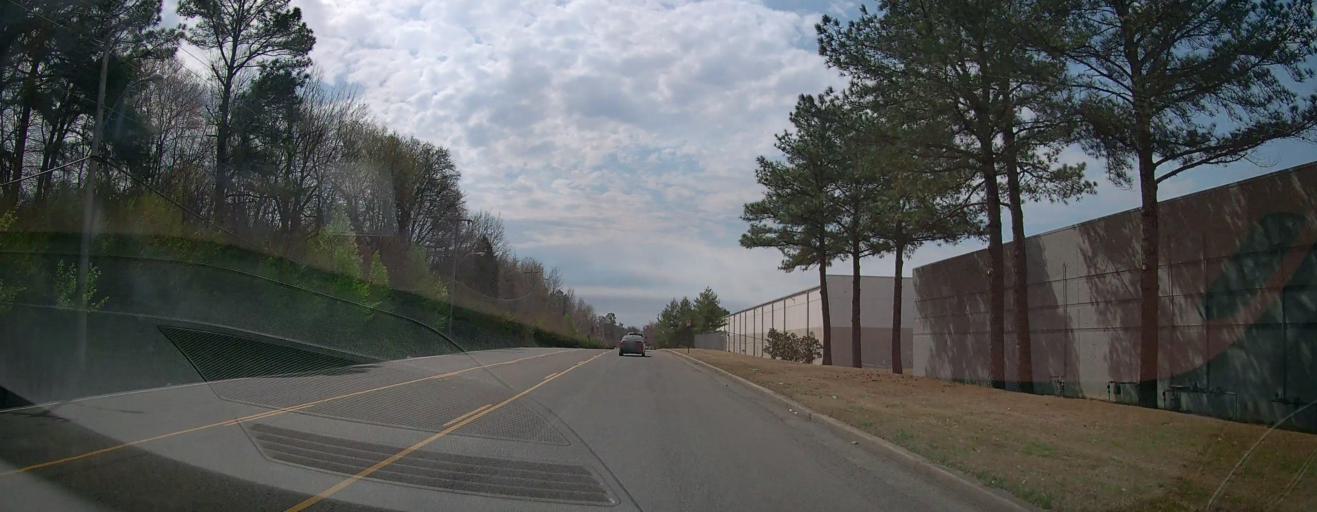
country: US
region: Mississippi
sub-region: De Soto County
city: Olive Branch
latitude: 35.0180
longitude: -89.8488
